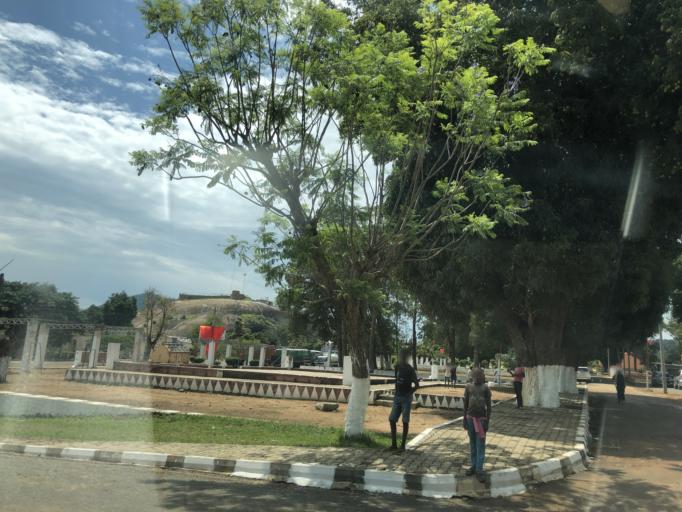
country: AO
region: Cuanza Sul
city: Quibala
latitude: -10.7361
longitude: 14.9794
